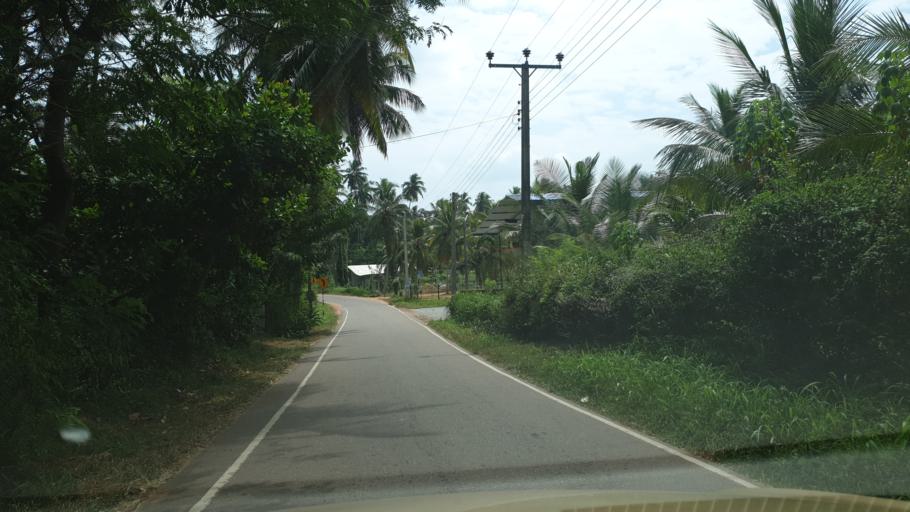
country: LK
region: North Western
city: Kuliyapitiya
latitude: 7.3484
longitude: 79.9794
